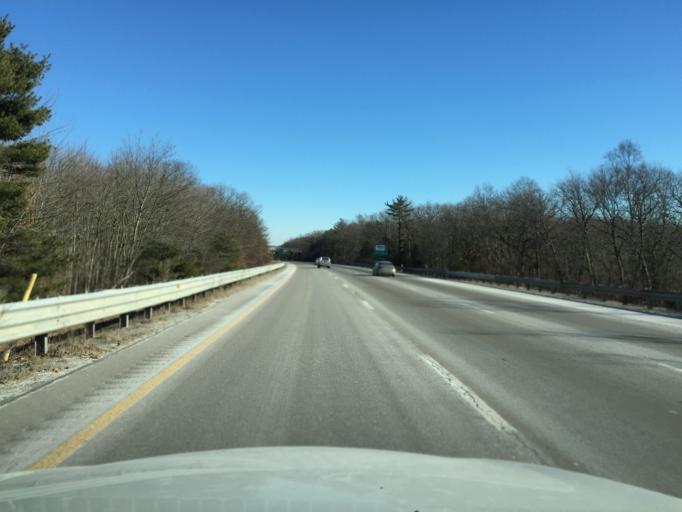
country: US
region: Massachusetts
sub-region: Norfolk County
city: Wrentham
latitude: 42.0374
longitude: -71.3262
